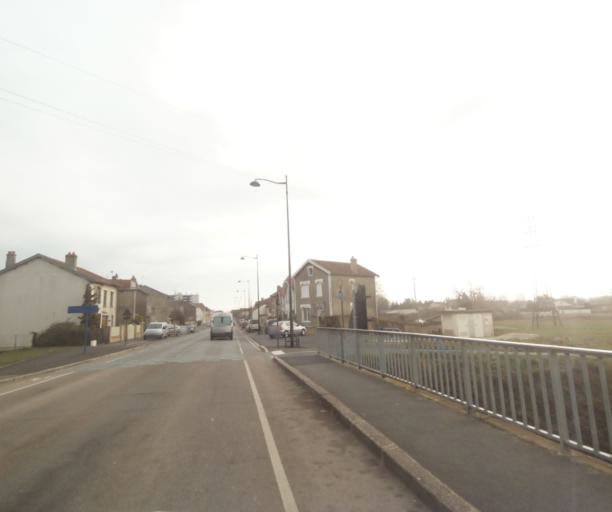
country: FR
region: Champagne-Ardenne
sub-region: Departement de la Haute-Marne
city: Saint-Dizier
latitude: 48.6386
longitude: 4.9267
